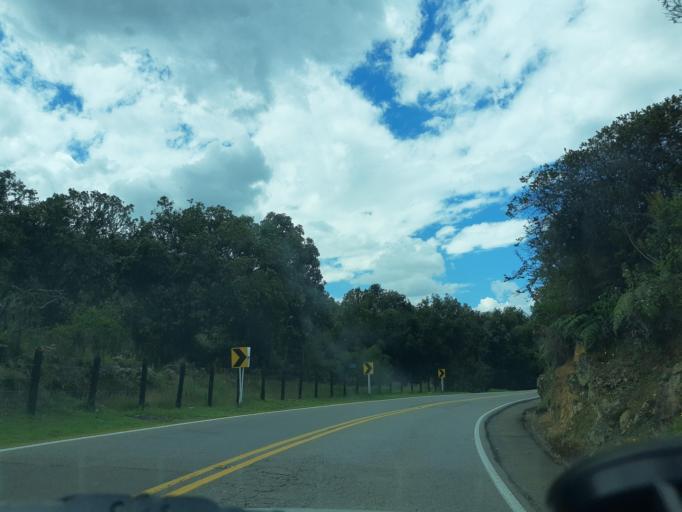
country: CO
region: Boyaca
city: Raquira
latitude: 5.5871
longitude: -73.7089
